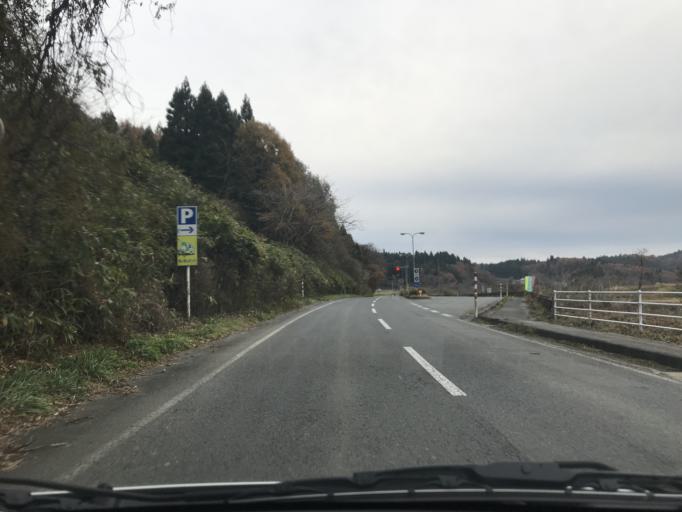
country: JP
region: Iwate
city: Kitakami
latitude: 39.2672
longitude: 141.2681
